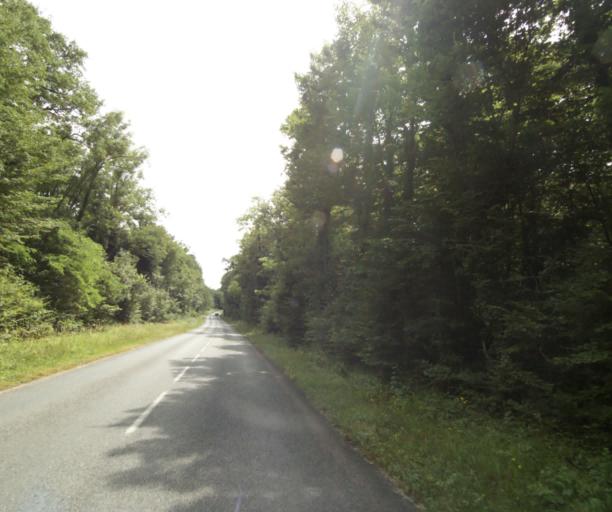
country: FR
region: Ile-de-France
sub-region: Departement de Seine-et-Marne
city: Chailly-en-Biere
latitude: 48.4874
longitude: 2.6286
